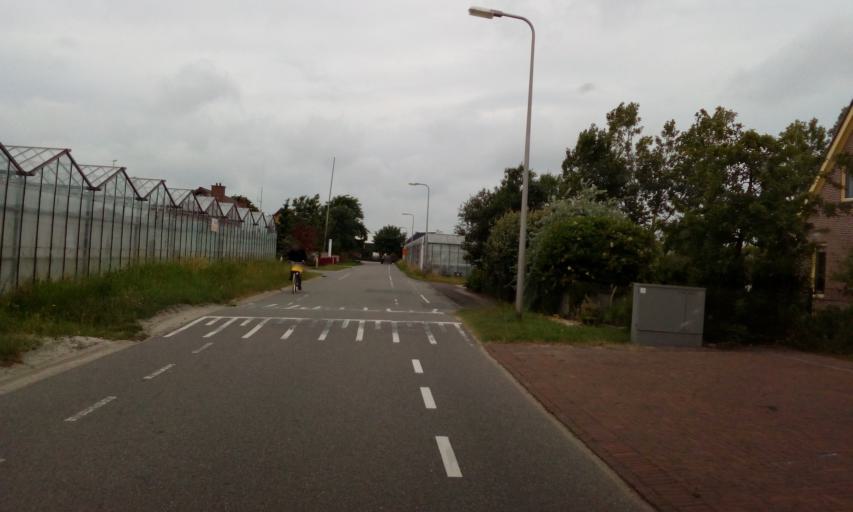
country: NL
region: South Holland
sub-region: Gemeente Westland
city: Monster
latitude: 52.0124
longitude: 4.1846
